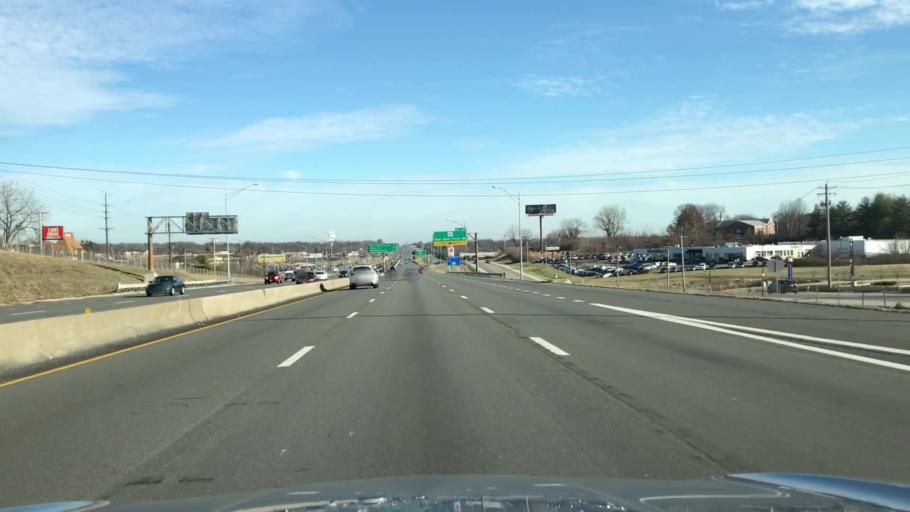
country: US
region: Missouri
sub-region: Saint Louis County
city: Dellwood
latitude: 38.7711
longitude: -90.2759
